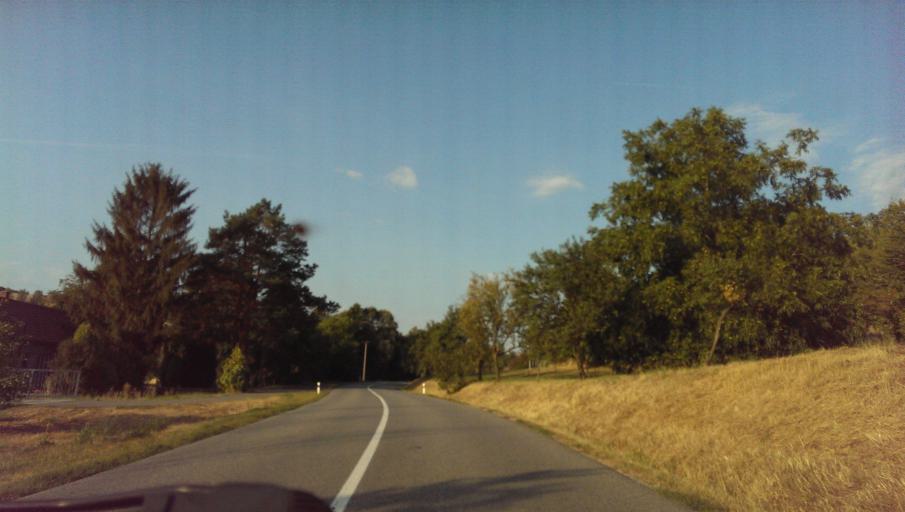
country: CZ
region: Zlin
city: Borsice
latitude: 49.0594
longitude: 17.3171
